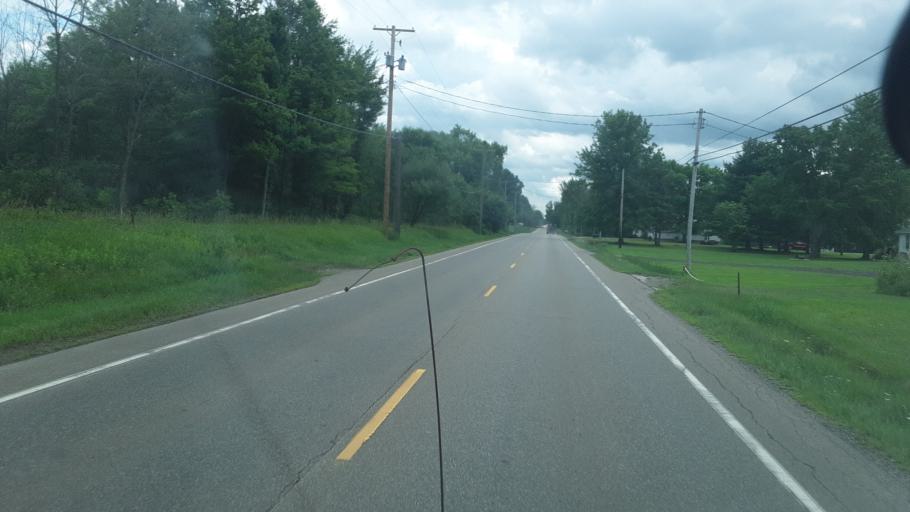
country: US
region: Ohio
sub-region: Ashtabula County
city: Jefferson
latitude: 41.7731
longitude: -80.7643
